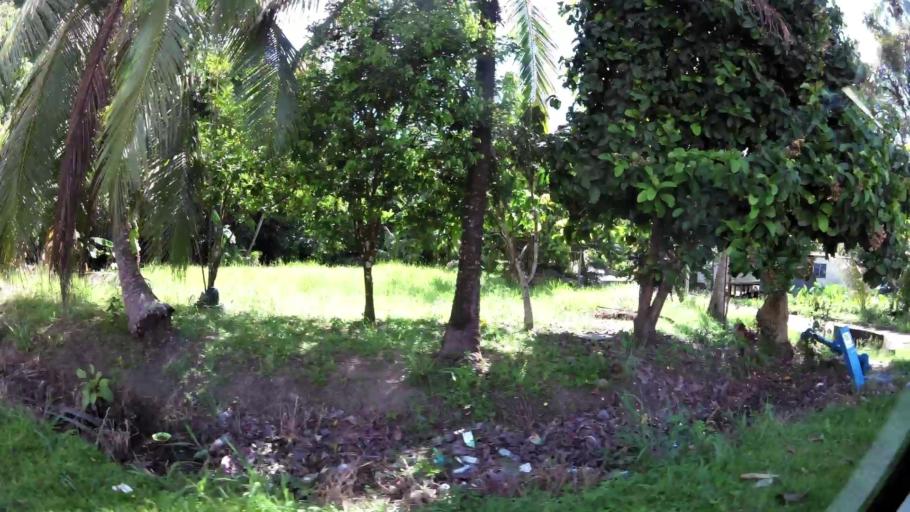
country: BN
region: Brunei and Muara
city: Bandar Seri Begawan
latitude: 5.0291
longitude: 115.0486
